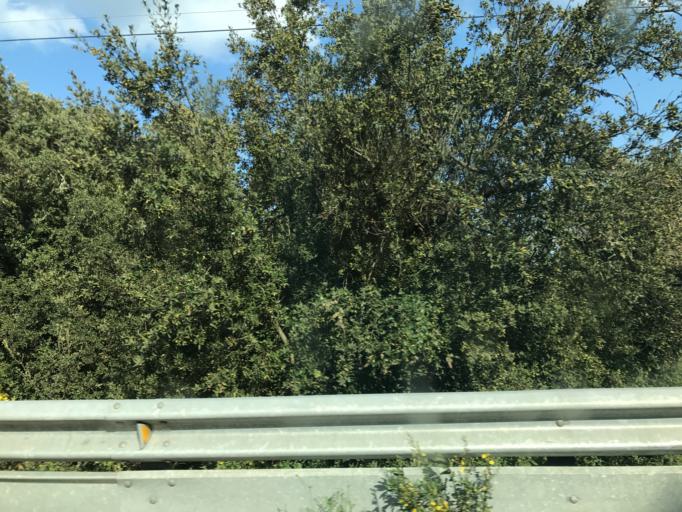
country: ES
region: Balearic Islands
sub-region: Illes Balears
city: Santa Margalida
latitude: 39.7270
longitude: 3.1991
